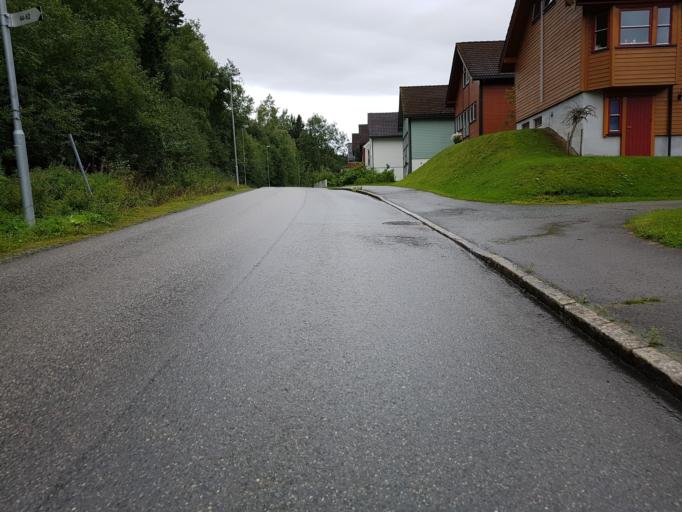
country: NO
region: Sor-Trondelag
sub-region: Trondheim
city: Trondheim
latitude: 63.4074
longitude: 10.4865
